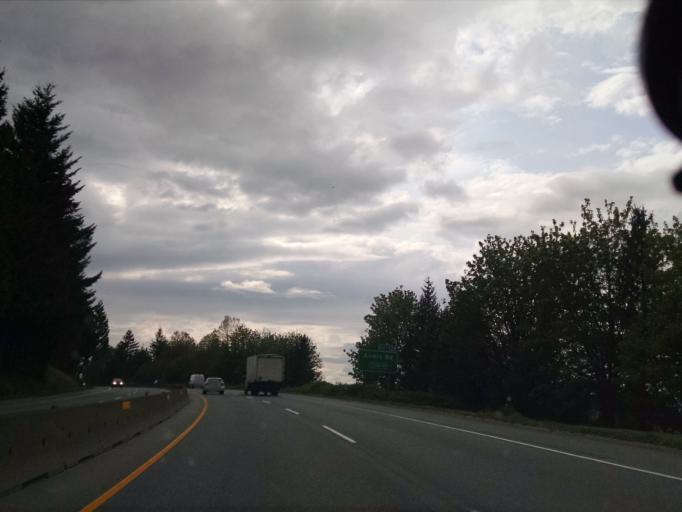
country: CA
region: British Columbia
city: Agassiz
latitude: 49.1604
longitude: -121.8095
